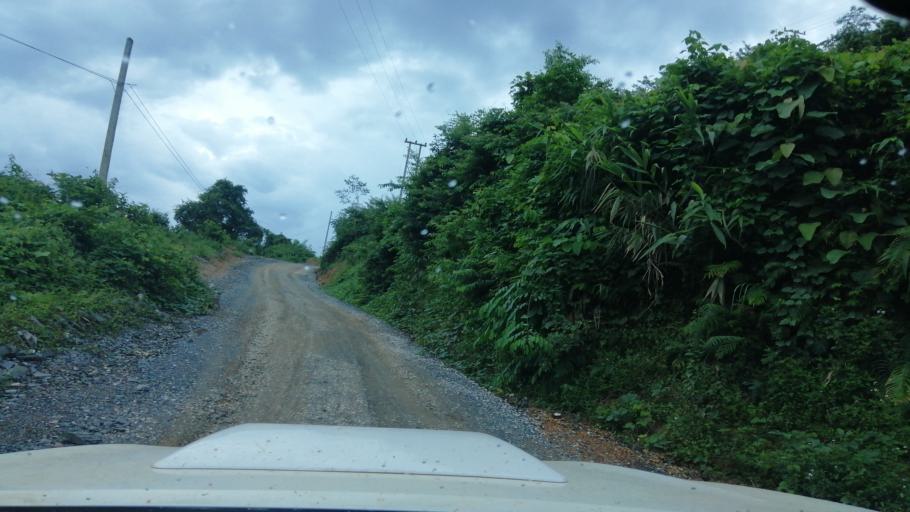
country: LA
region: Xiagnabouli
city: Sainyabuli
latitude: 19.1894
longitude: 101.7866
